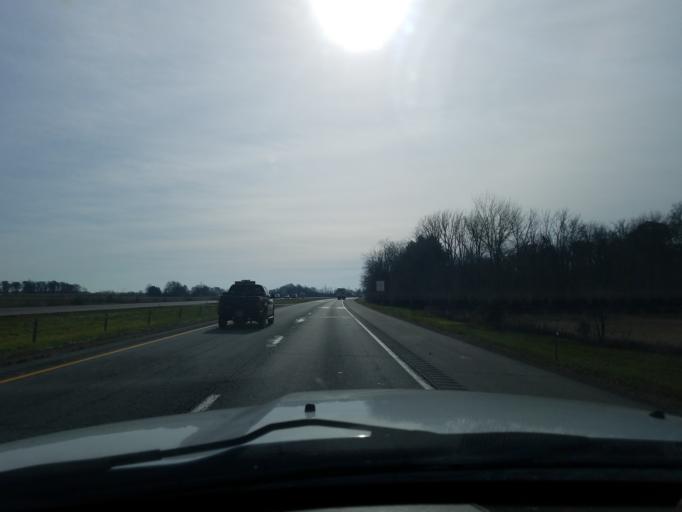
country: US
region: Indiana
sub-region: Delaware County
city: Daleville
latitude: 40.1003
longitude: -85.5691
